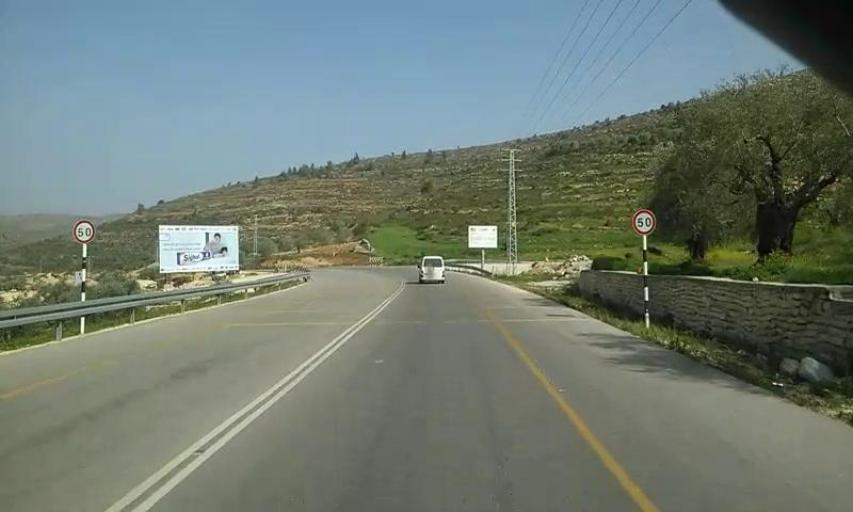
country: PS
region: West Bank
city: Dura al Qar`
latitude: 31.9813
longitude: 35.2350
